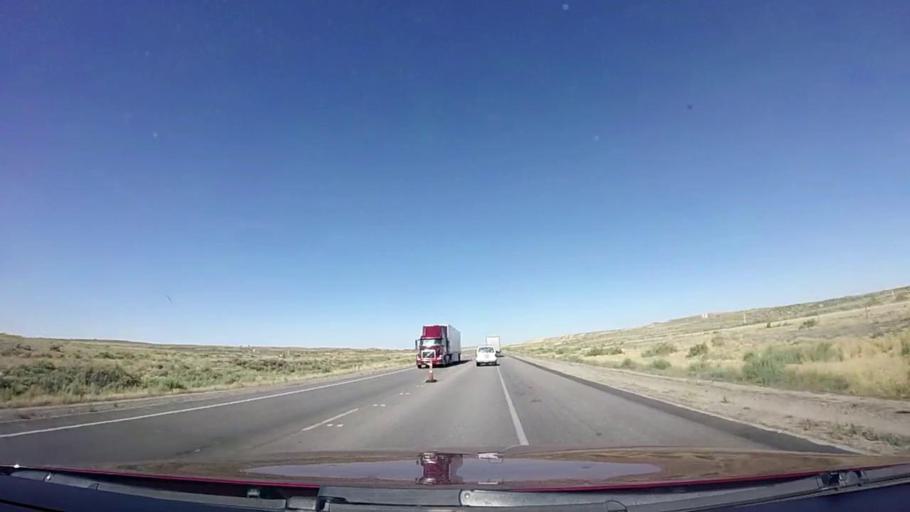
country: US
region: Wyoming
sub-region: Carbon County
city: Rawlins
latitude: 41.7060
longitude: -107.8543
